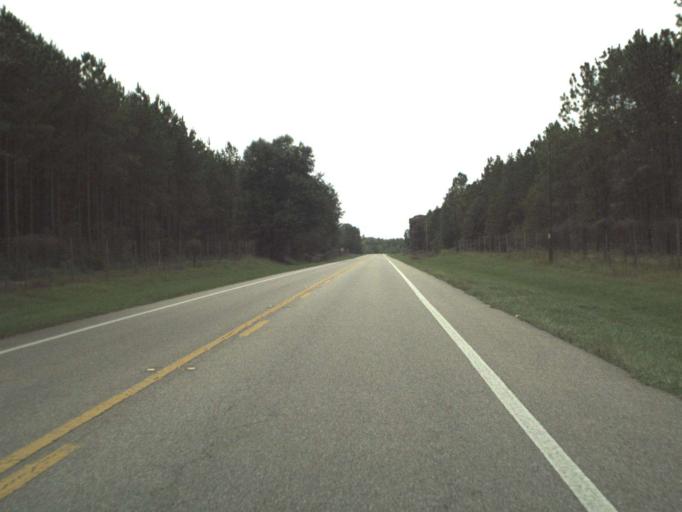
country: US
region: Florida
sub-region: Calhoun County
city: Blountstown
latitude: 30.5911
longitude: -85.0255
